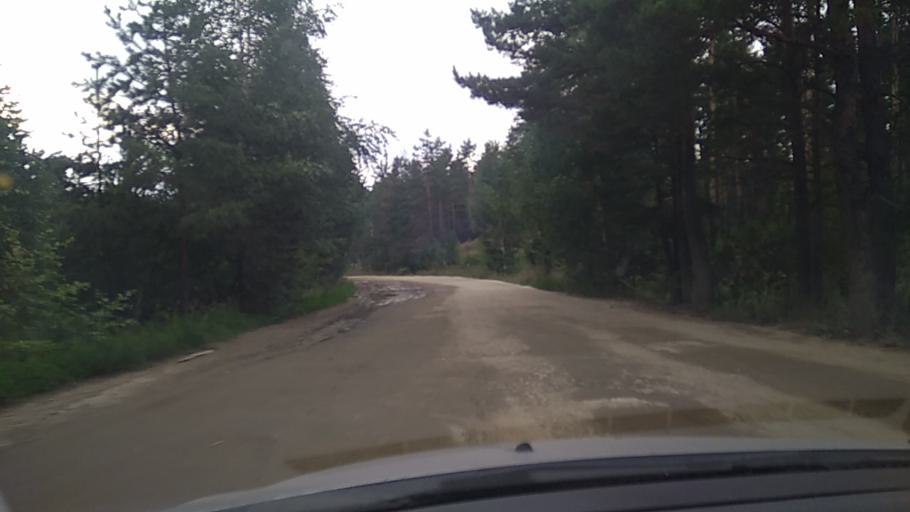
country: RU
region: Chelyabinsk
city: Kyshtym
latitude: 55.6856
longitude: 60.5678
